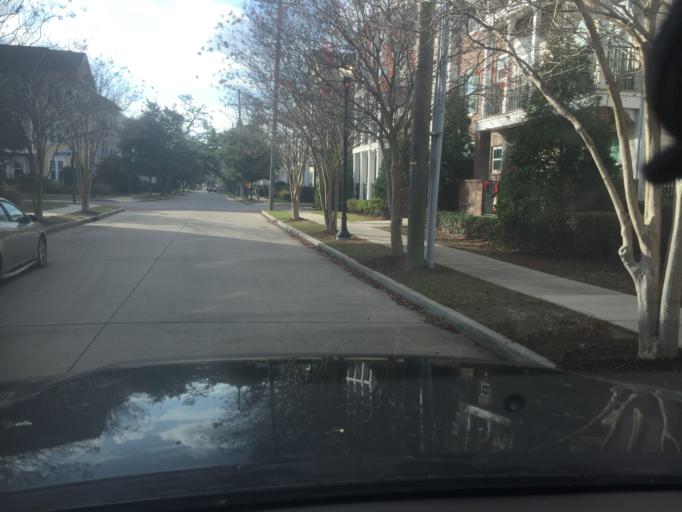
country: US
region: Louisiana
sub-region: Orleans Parish
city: New Orleans
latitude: 29.9954
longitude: -90.0756
